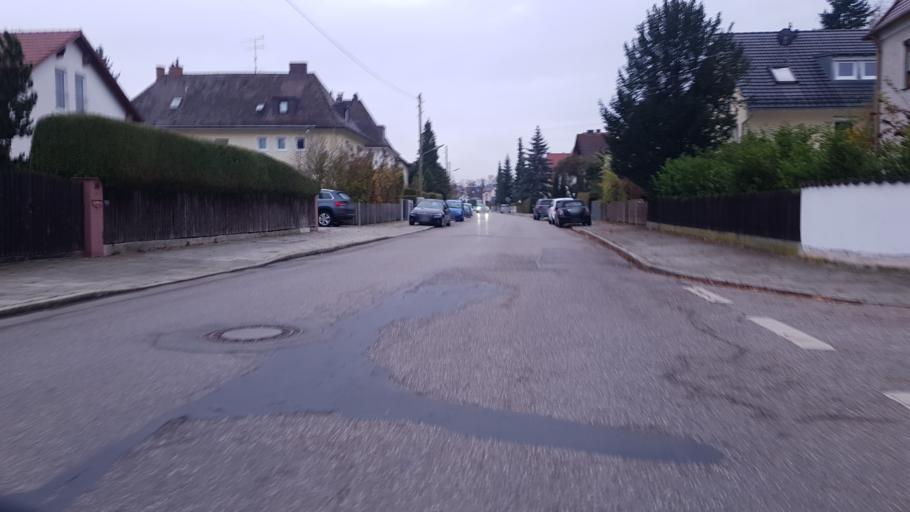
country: DE
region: Bavaria
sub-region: Upper Bavaria
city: Bogenhausen
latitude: 48.1145
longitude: 11.6258
